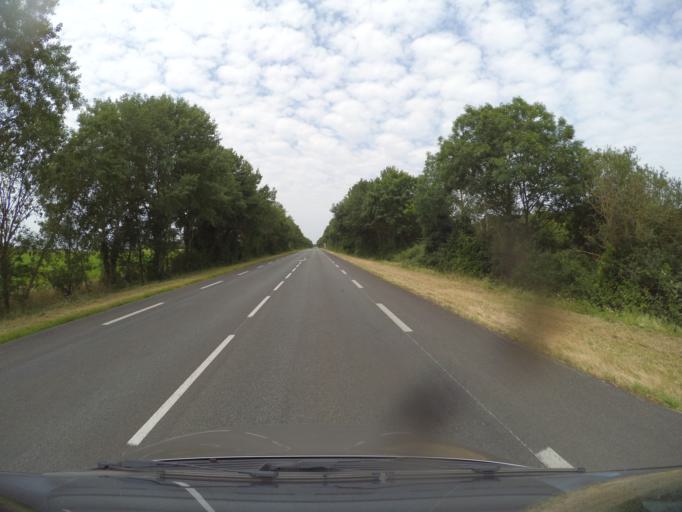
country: FR
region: Pays de la Loire
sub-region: Departement de la Vendee
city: Saint-Georges-de-Montaigu
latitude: 46.9354
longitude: -1.3206
